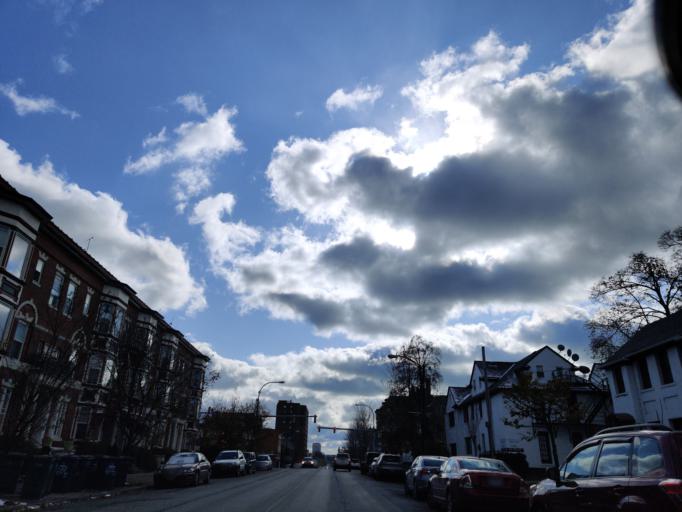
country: US
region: New York
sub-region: Erie County
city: Buffalo
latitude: 42.9138
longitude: -78.8771
